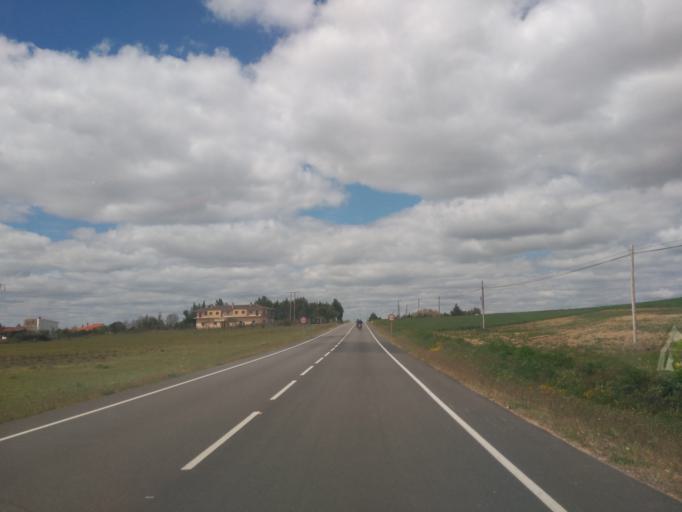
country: ES
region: Castille and Leon
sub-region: Provincia de Salamanca
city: Villamayor
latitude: 41.0051
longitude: -5.7026
